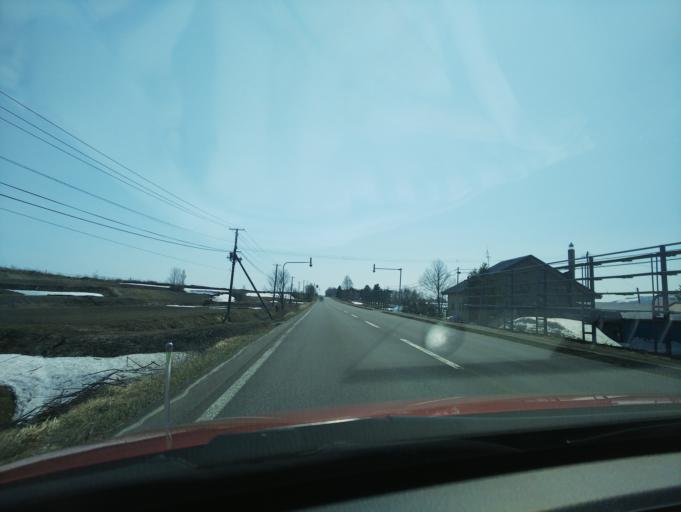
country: JP
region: Hokkaido
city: Nayoro
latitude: 44.2594
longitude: 142.3945
